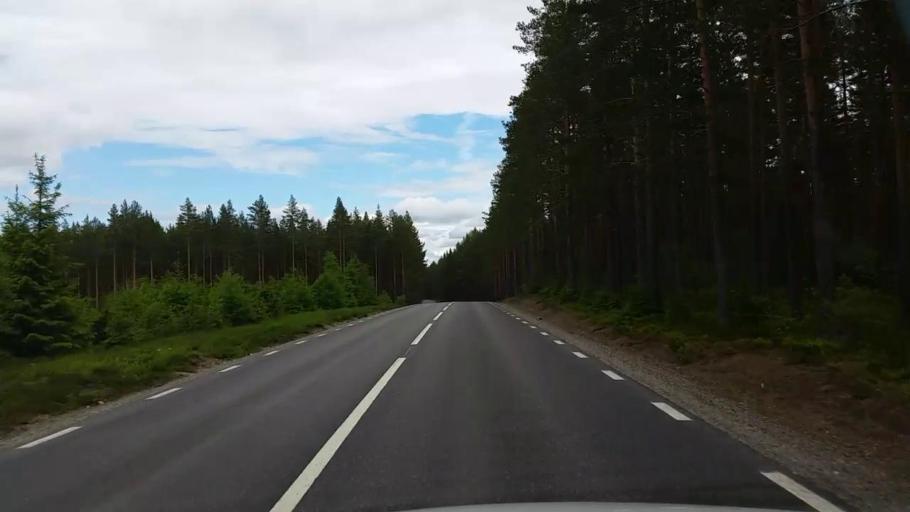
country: SE
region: Gaevleborg
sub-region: Sandvikens Kommun
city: Jarbo
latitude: 60.9528
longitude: 16.3997
